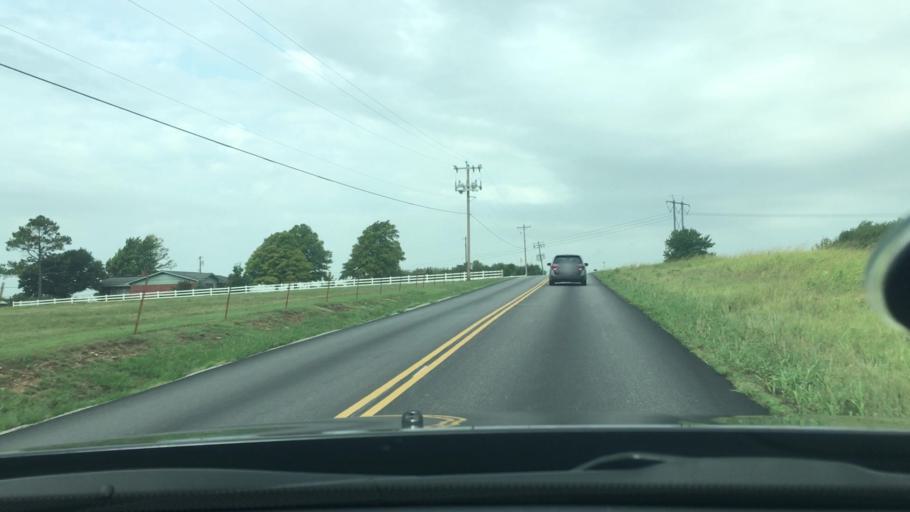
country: US
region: Oklahoma
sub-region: Carter County
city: Ardmore
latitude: 34.2020
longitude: -97.1915
